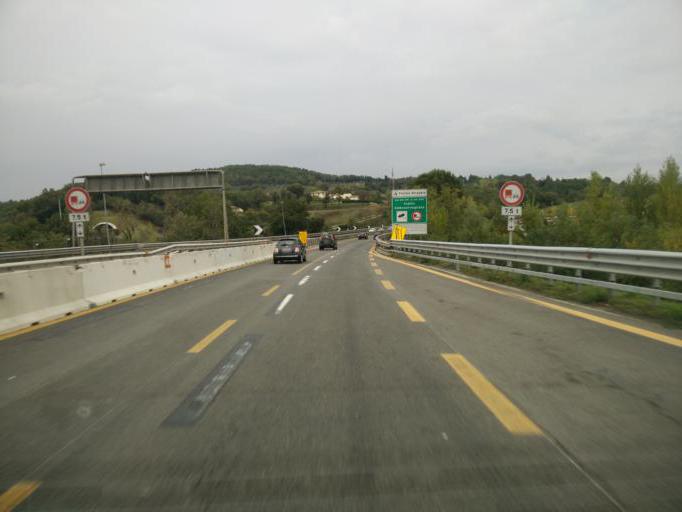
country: IT
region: Tuscany
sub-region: Province of Florence
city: Cavallina
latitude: 43.9865
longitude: 11.2116
